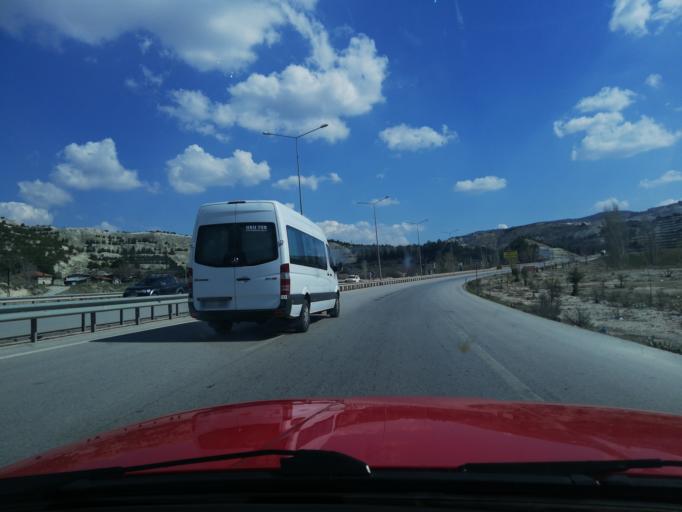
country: TR
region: Burdur
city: Burdur
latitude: 37.7079
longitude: 30.3046
